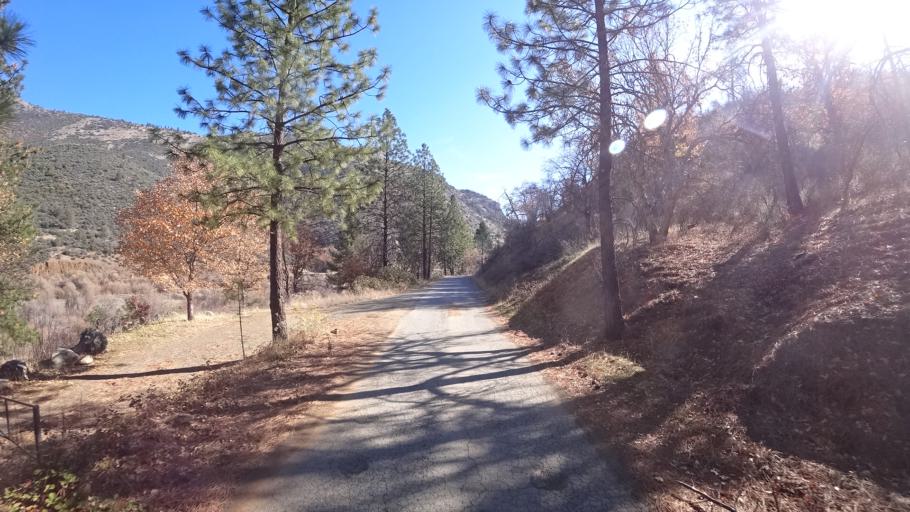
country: US
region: California
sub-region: Siskiyou County
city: Yreka
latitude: 41.8403
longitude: -122.6733
